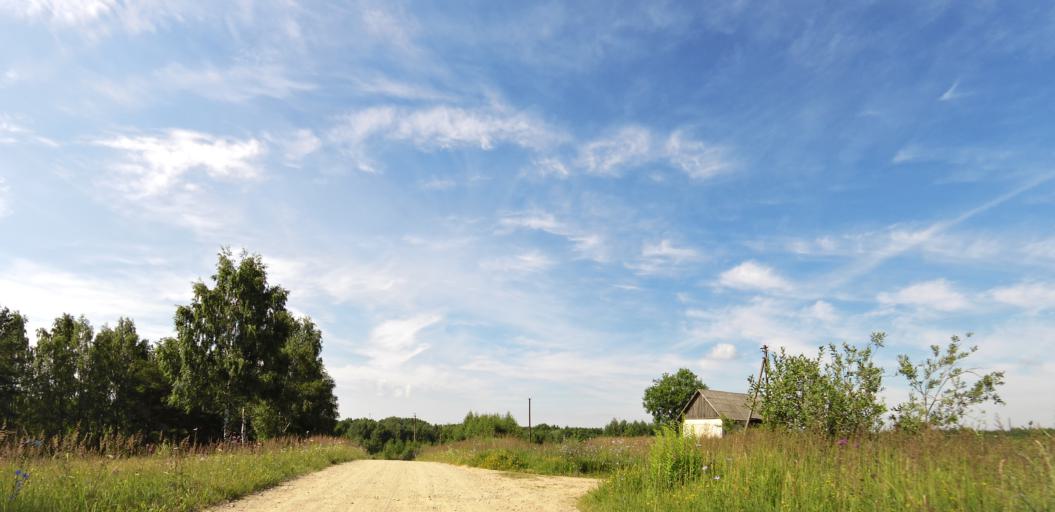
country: LT
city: Grigiskes
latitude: 54.7773
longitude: 25.0646
